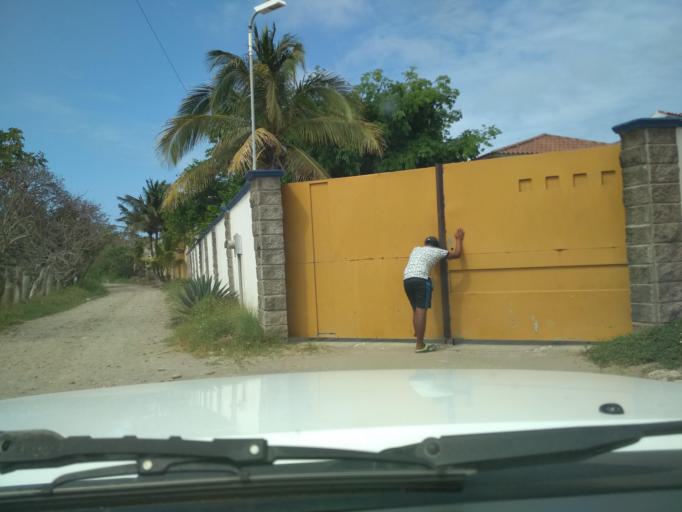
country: MX
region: Veracruz
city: Anton Lizardo
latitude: 19.0246
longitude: -95.9680
